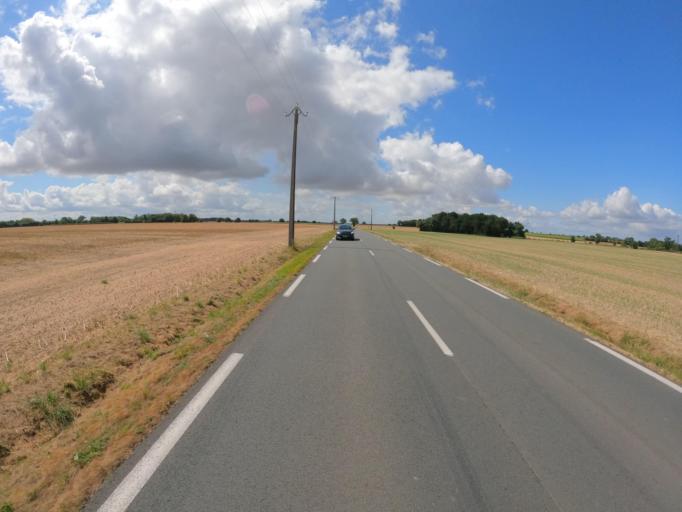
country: FR
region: Pays de la Loire
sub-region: Departement de Maine-et-Loire
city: Saint-Laurent-des-Autels
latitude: 47.2583
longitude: -1.2038
